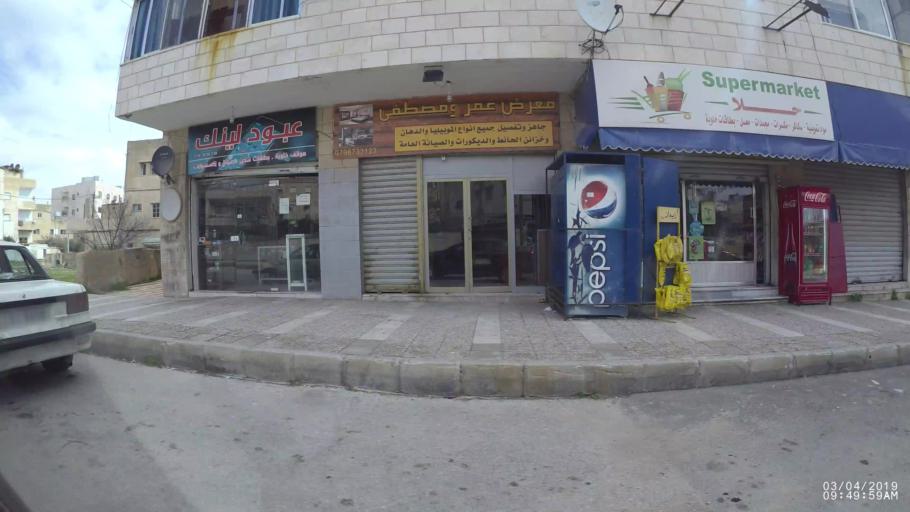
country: JO
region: Amman
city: Wadi as Sir
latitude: 31.9514
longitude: 35.8348
